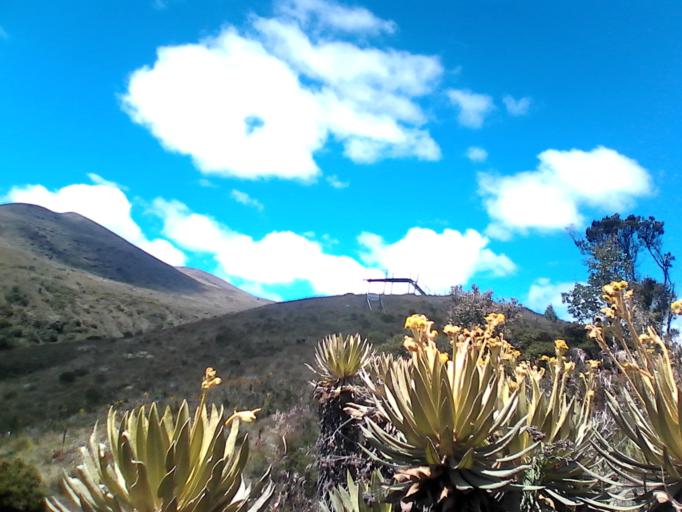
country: CO
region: Boyaca
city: Santa Rosa de Viterbo
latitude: 5.9119
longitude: -73.0511
